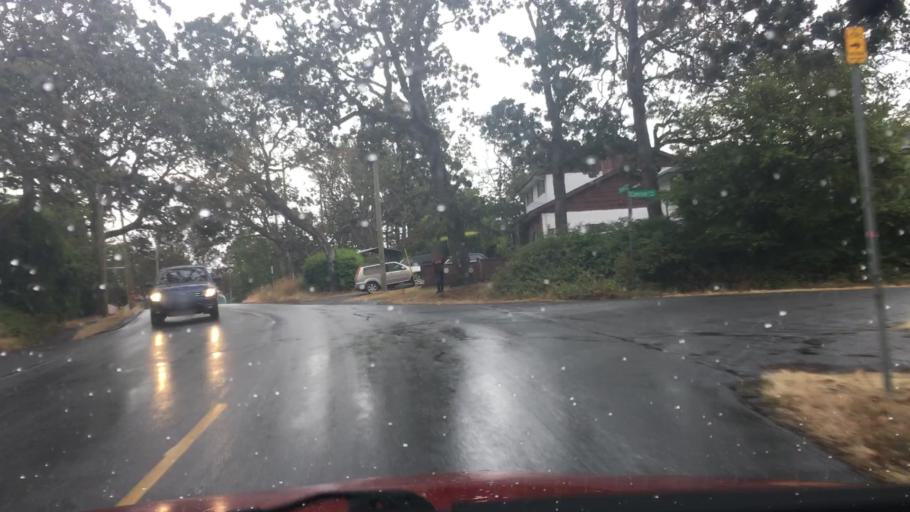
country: CA
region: British Columbia
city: Victoria
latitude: 48.4547
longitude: -123.3509
